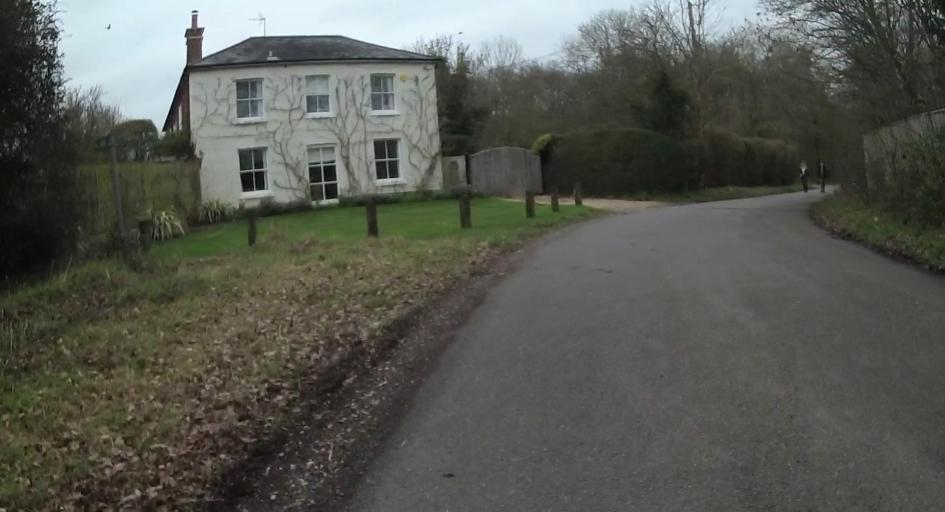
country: GB
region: England
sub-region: West Berkshire
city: Stratfield Mortimer
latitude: 51.3866
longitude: -1.0405
